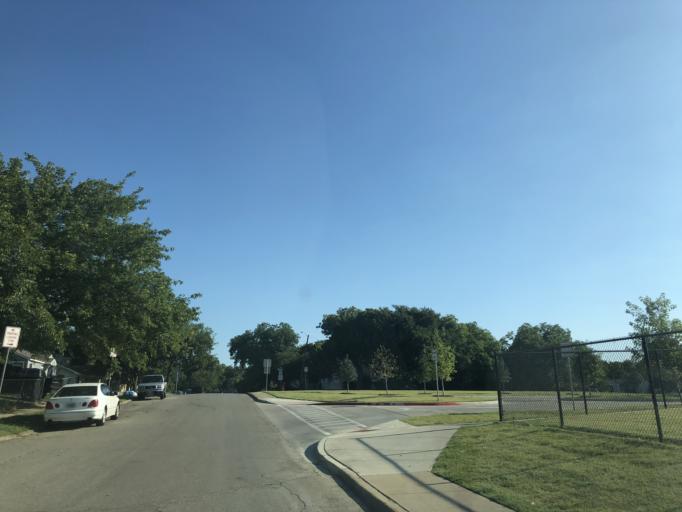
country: US
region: Texas
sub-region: Dallas County
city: Grand Prairie
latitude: 32.7373
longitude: -97.0080
